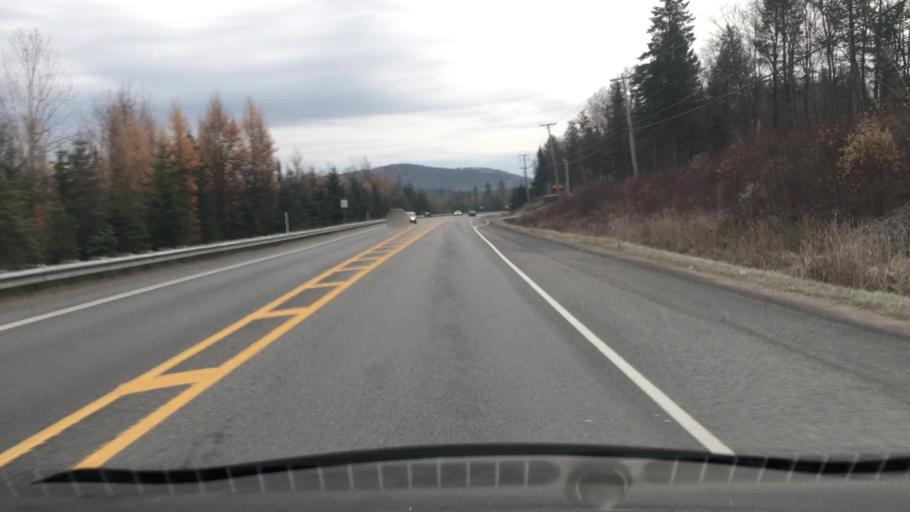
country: CA
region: Quebec
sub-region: Laurentides
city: Saint-Sauveur
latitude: 45.9000
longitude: -74.2205
